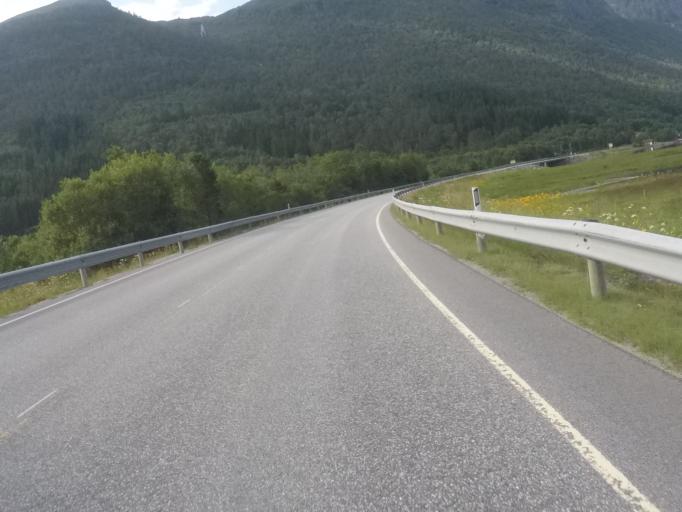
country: NO
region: More og Romsdal
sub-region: Rauma
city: Andalsnes
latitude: 62.5735
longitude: 7.7885
